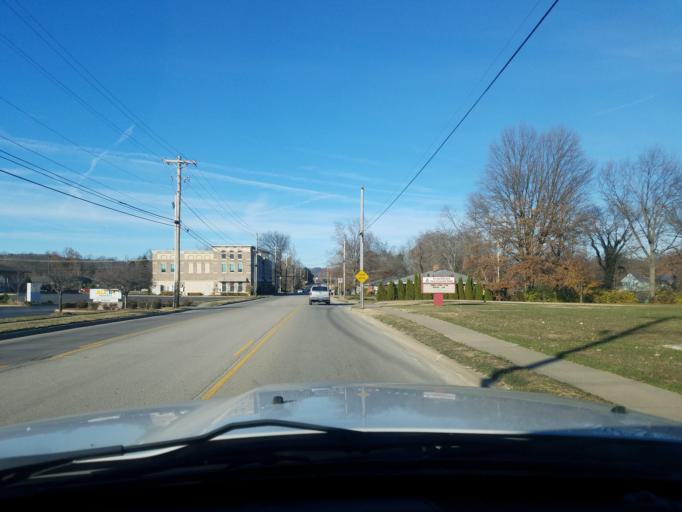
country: US
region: Indiana
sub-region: Floyd County
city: New Albany
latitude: 38.3084
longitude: -85.8365
